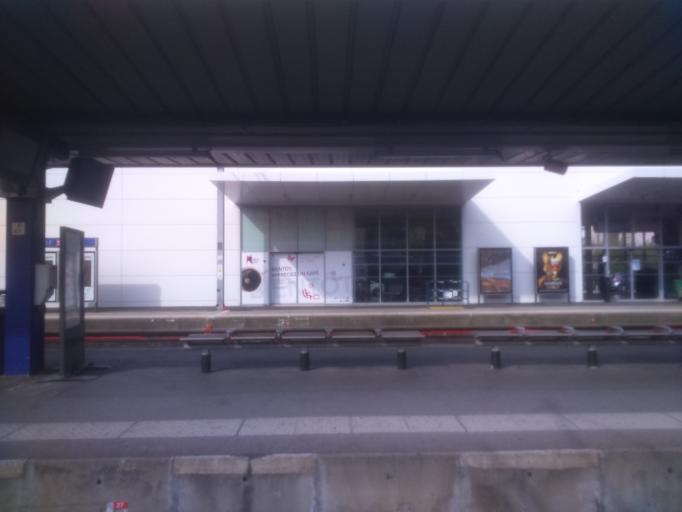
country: FR
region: Rhone-Alpes
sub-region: Departement de l'Isere
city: Saint-Martin-le-Vinoux
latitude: 45.1912
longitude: 5.7140
